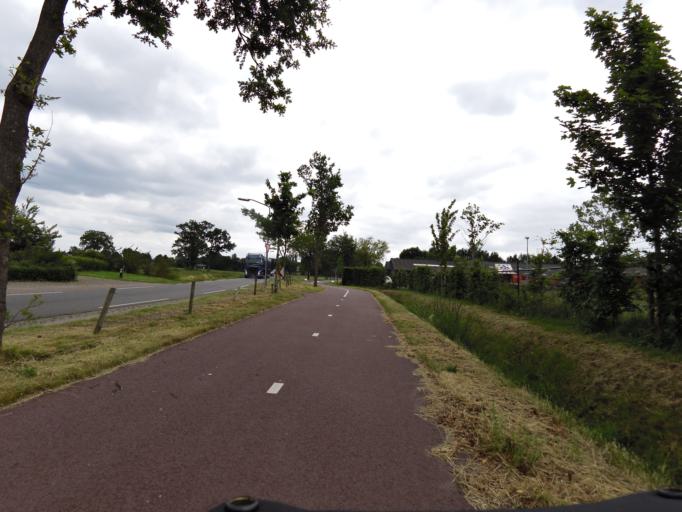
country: BE
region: Flanders
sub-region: Provincie Antwerpen
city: Baarle-Hertog
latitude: 51.4601
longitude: 4.8480
